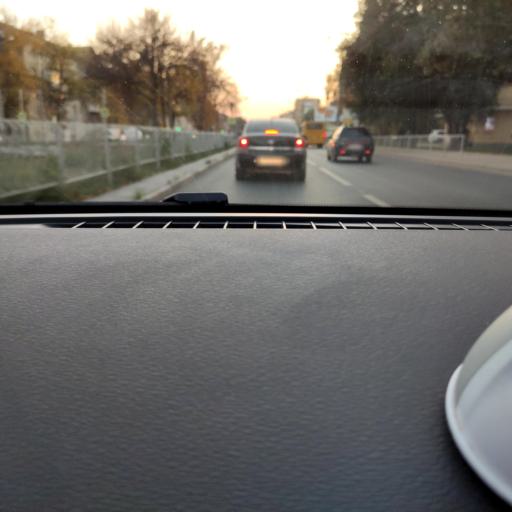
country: RU
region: Samara
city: Samara
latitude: 53.2148
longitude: 50.2526
